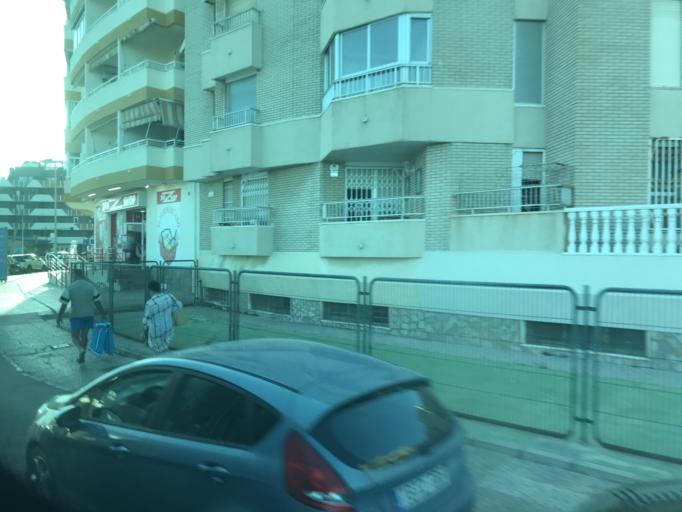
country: ES
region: Valencia
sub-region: Provincia de Alicante
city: Torrevieja
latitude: 37.9810
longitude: -0.6632
